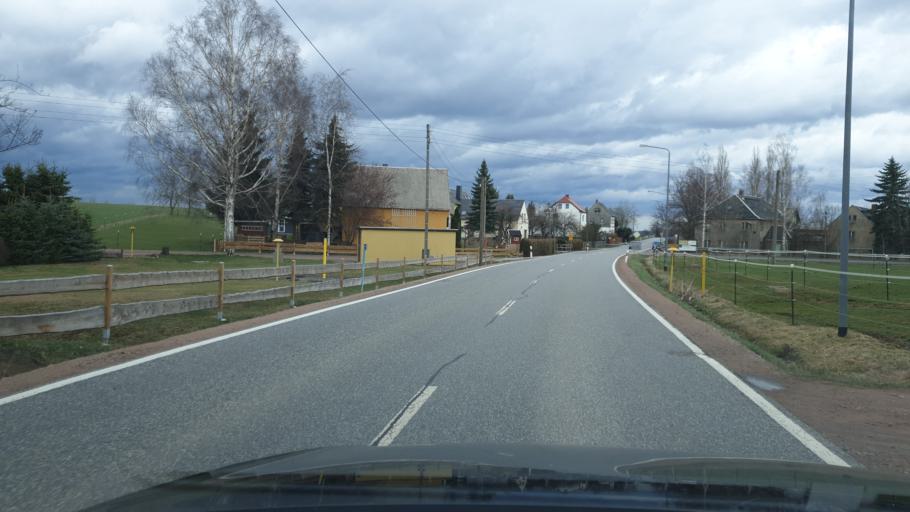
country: DE
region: Saxony
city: Altmittweida
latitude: 50.9564
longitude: 12.9201
